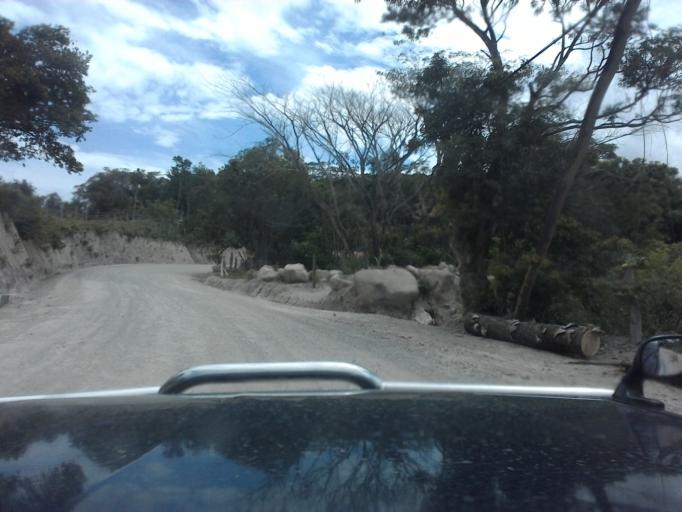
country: CR
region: Guanacaste
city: Juntas
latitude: 10.2395
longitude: -84.8522
